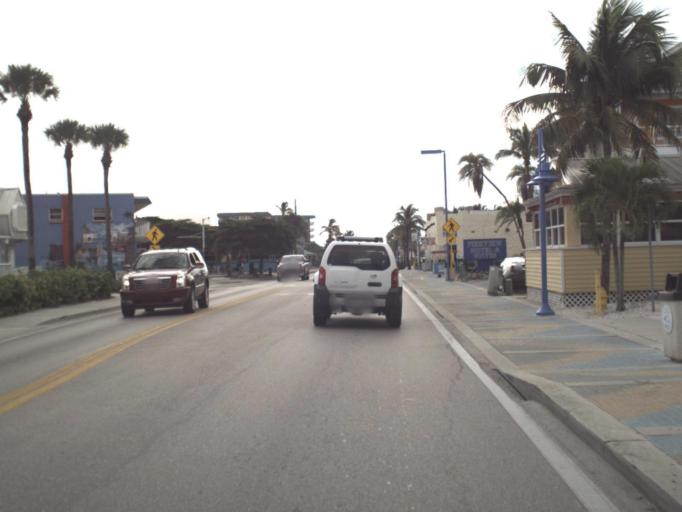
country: US
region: Florida
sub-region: Lee County
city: Fort Myers Beach
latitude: 26.4526
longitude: -81.9544
